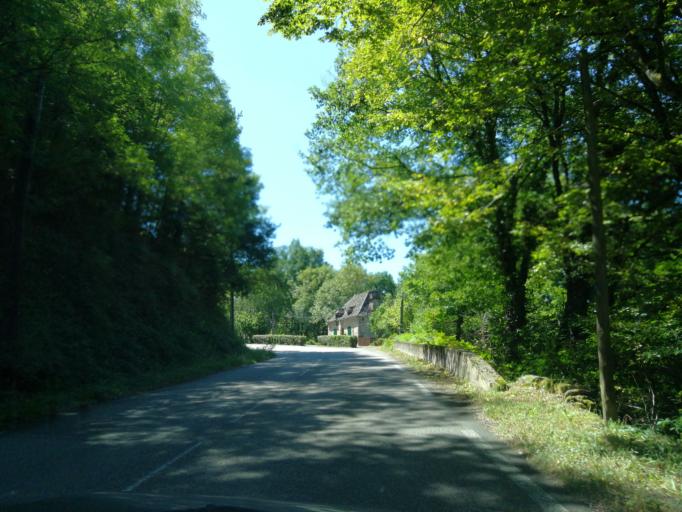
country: FR
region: Limousin
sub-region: Departement de la Correze
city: Argentat
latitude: 45.0783
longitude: 1.9446
